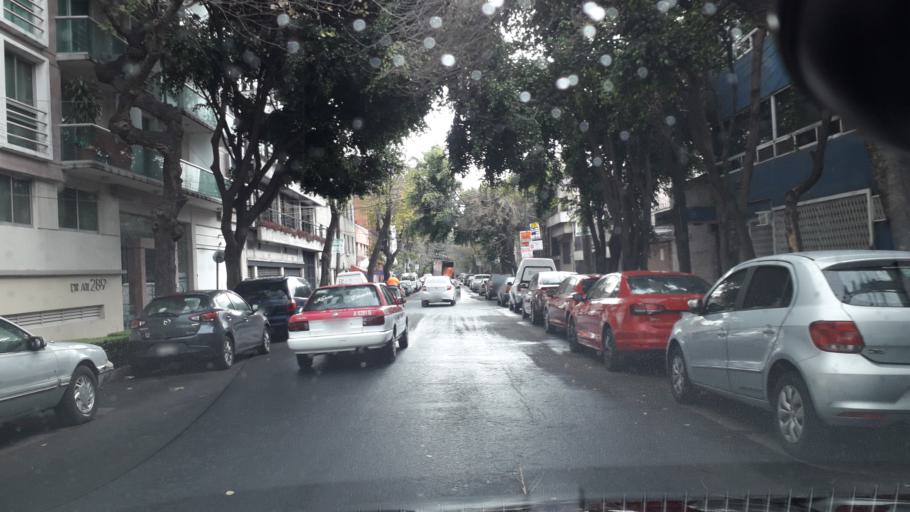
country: MX
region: Mexico City
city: Cuauhtemoc
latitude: 19.4544
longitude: -99.1553
